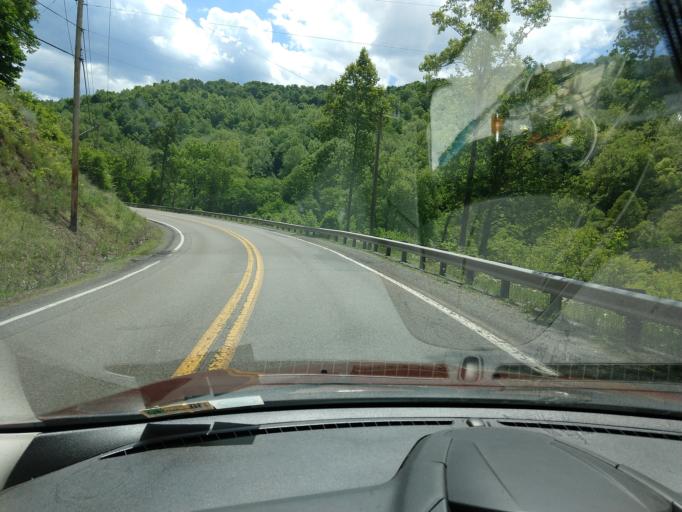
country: US
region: West Virginia
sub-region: Gilmer County
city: Glenville
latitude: 38.8651
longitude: -80.6723
